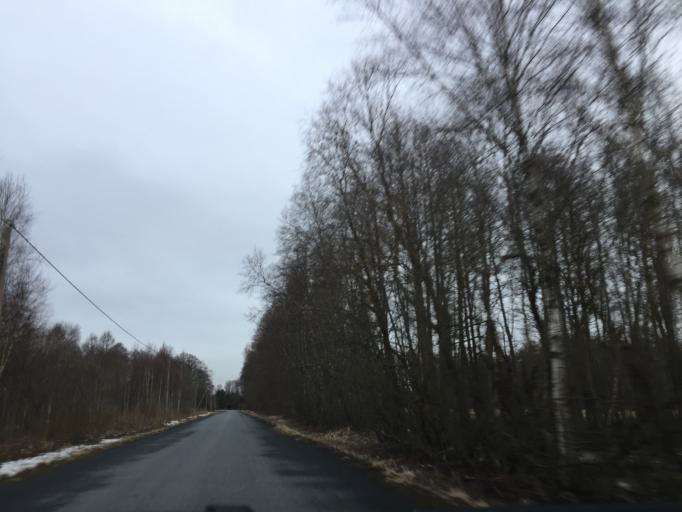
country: EE
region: Laeaene
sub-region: Haapsalu linn
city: Haapsalu
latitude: 58.7971
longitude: 23.4906
